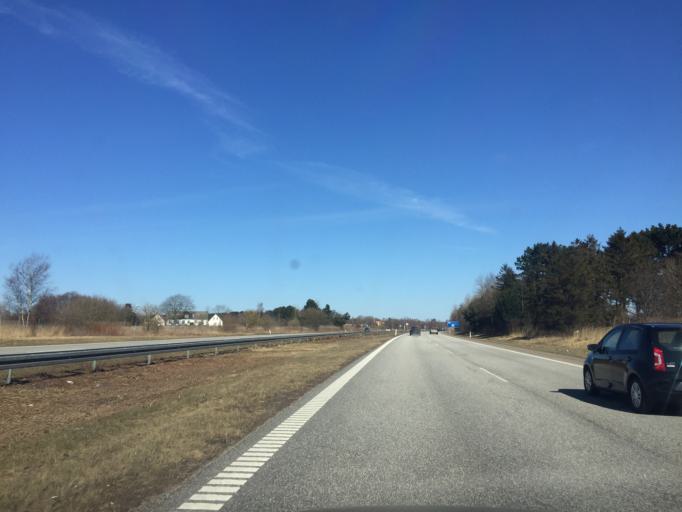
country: DK
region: Capital Region
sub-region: Fredensborg Kommune
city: Niva
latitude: 55.9575
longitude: 12.4817
